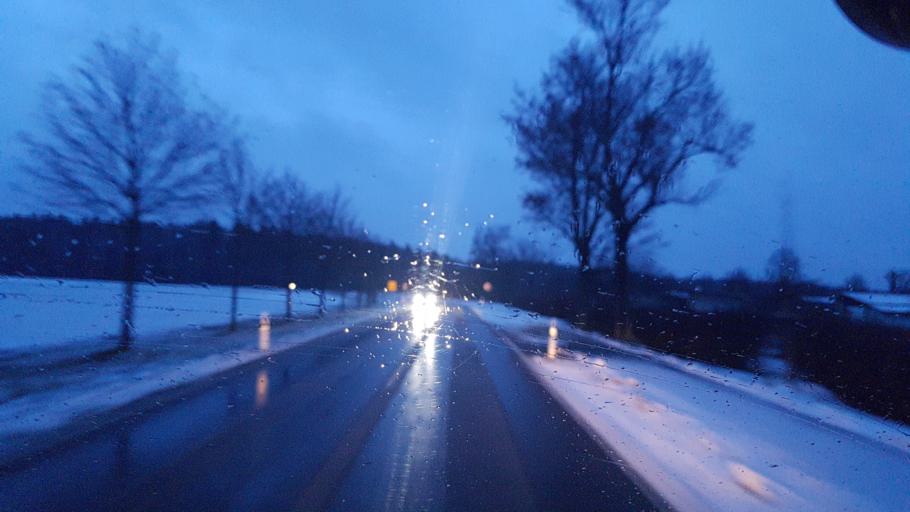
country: DE
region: Brandenburg
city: Briesen
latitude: 51.8057
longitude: 14.2486
